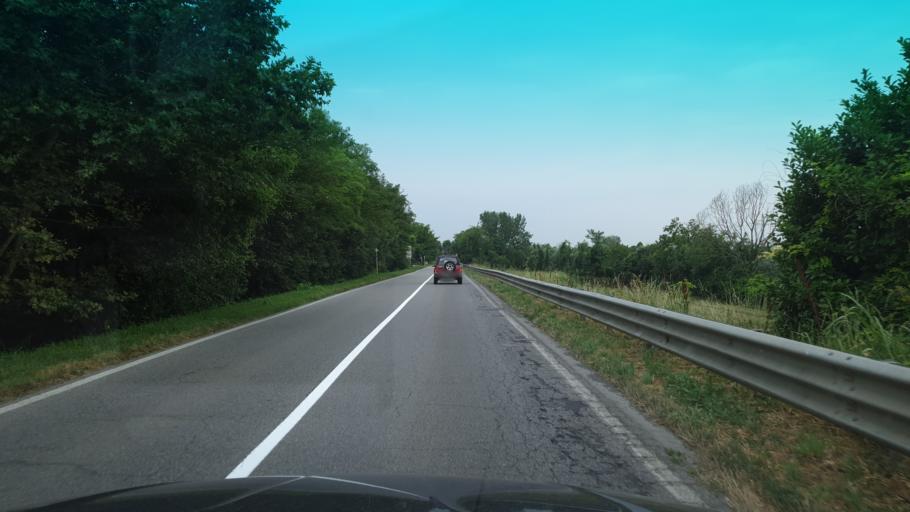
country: IT
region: Lombardy
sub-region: Provincia di Bergamo
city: Badalasco
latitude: 45.5324
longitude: 9.5380
